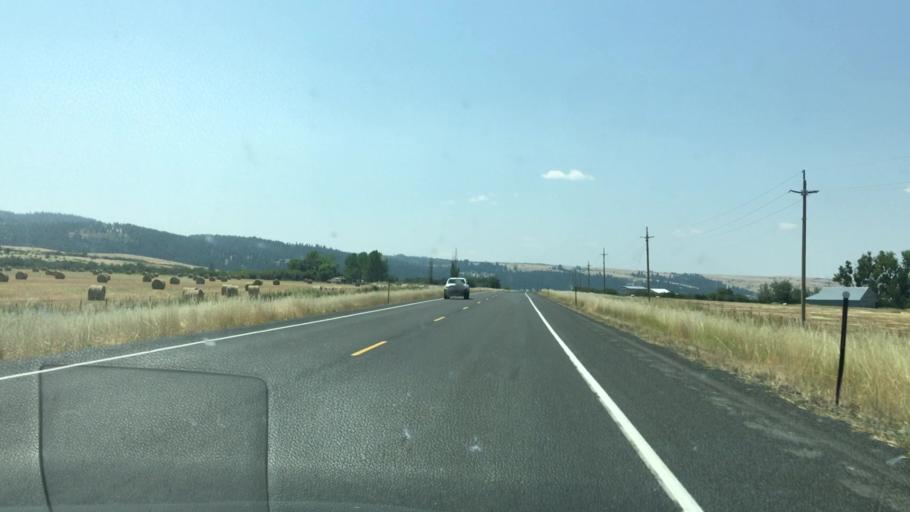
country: US
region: Idaho
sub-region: Idaho County
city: Grangeville
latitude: 45.9005
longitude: -116.1798
